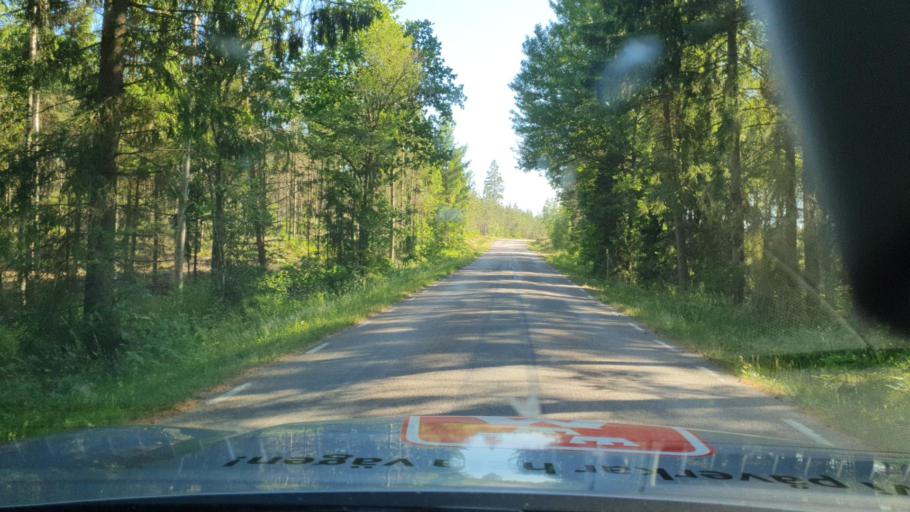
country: SE
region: Kalmar
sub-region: Torsas Kommun
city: Torsas
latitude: 56.4914
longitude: 16.1011
